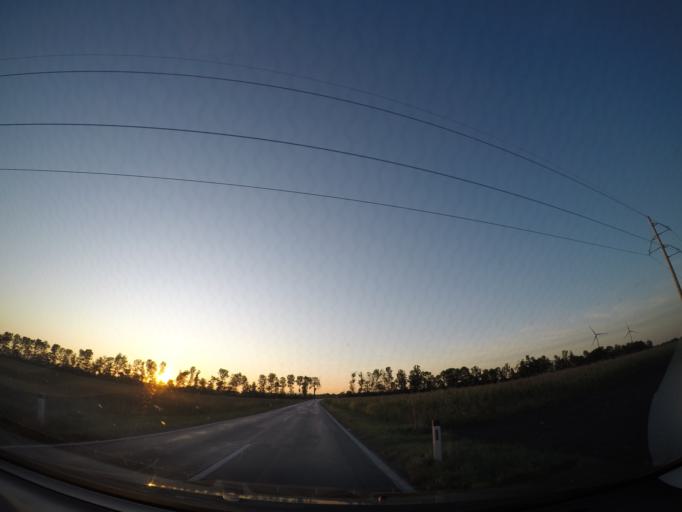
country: AT
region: Lower Austria
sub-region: Politischer Bezirk Bruck an der Leitha
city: Au am Leithaberge
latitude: 47.9470
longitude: 16.5542
